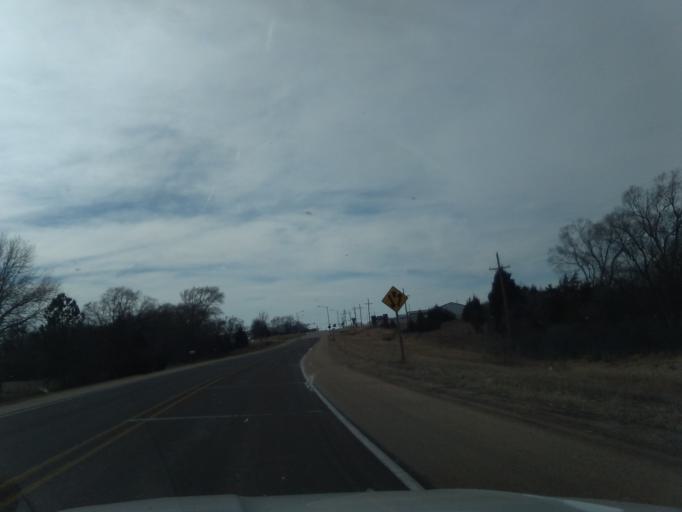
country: US
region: Nebraska
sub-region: Jefferson County
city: Fairbury
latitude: 40.1466
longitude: -97.1657
